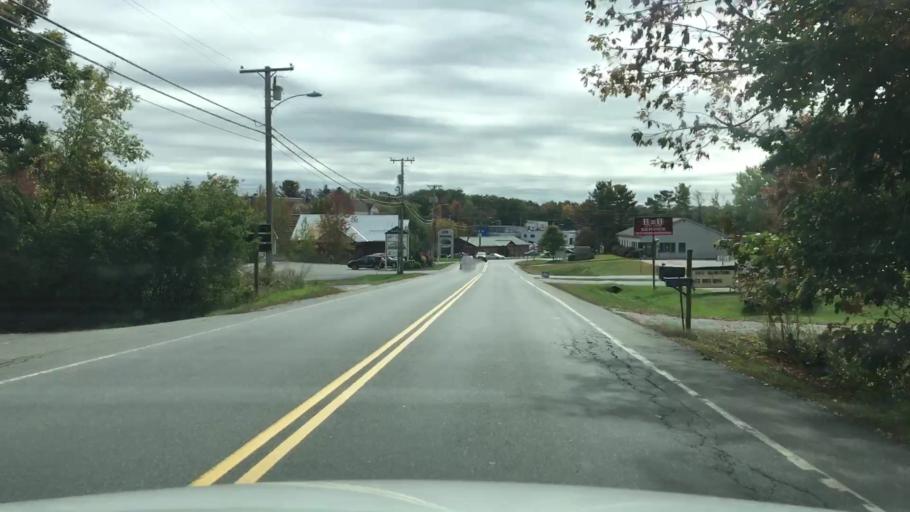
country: US
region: Maine
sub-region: Kennebec County
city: Waterville
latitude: 44.5473
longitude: -69.6760
